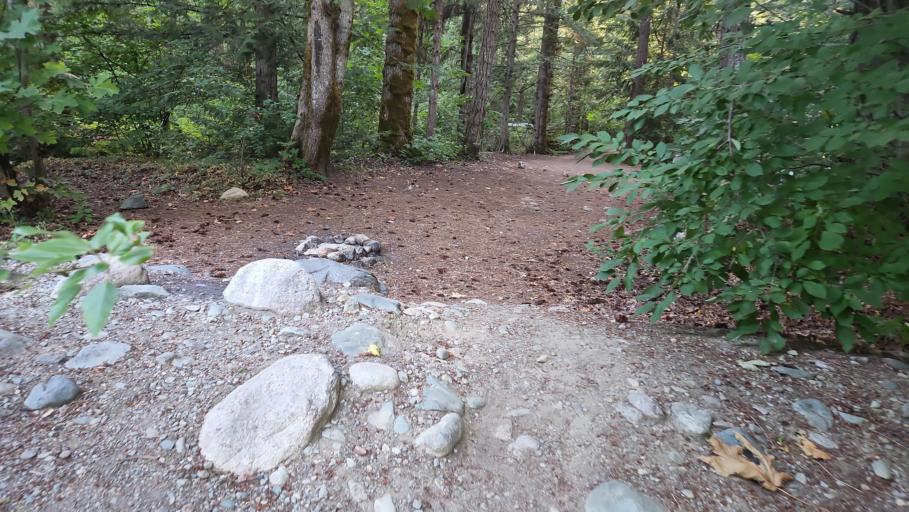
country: CA
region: British Columbia
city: Pemberton
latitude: 50.3494
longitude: -122.7289
